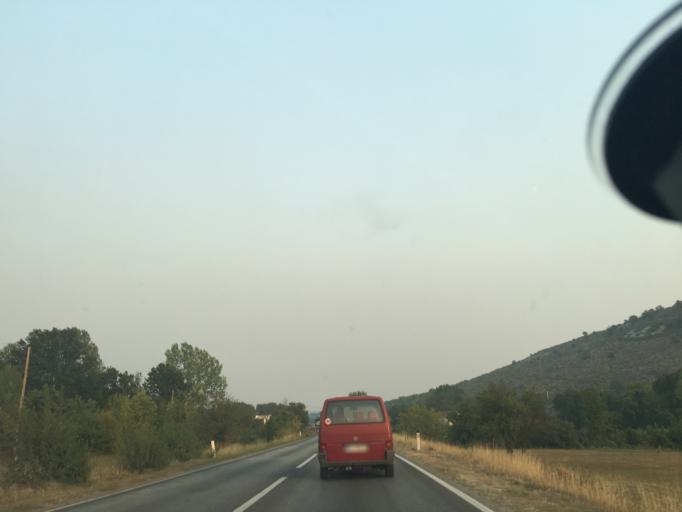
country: ME
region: Danilovgrad
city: Danilovgrad
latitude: 42.5098
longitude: 19.1313
